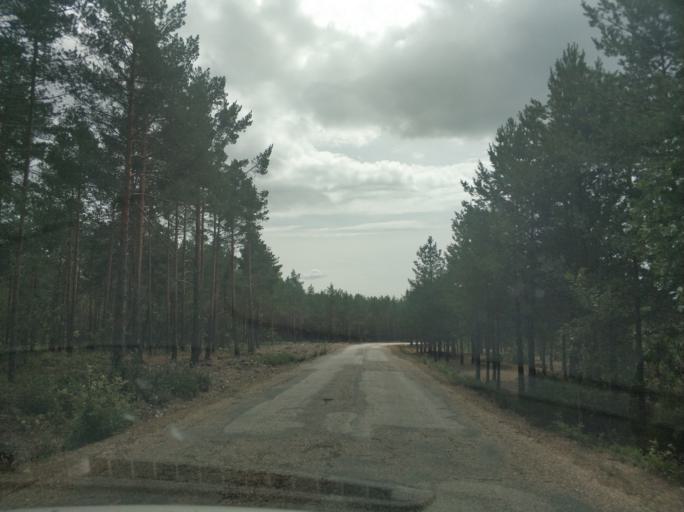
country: ES
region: Castille and Leon
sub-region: Provincia de Soria
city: Duruelo de la Sierra
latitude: 41.9582
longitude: -2.9198
